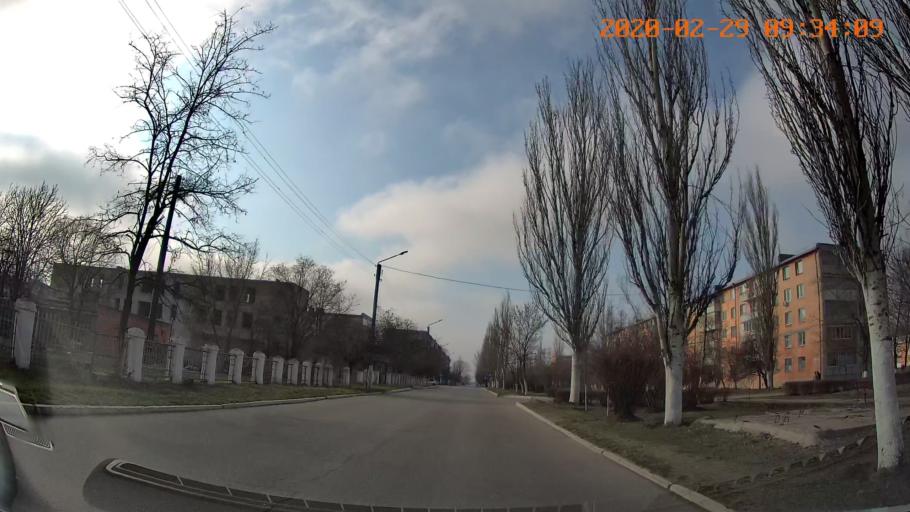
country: MD
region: Telenesti
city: Dnestrovsc
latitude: 46.6257
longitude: 29.9043
